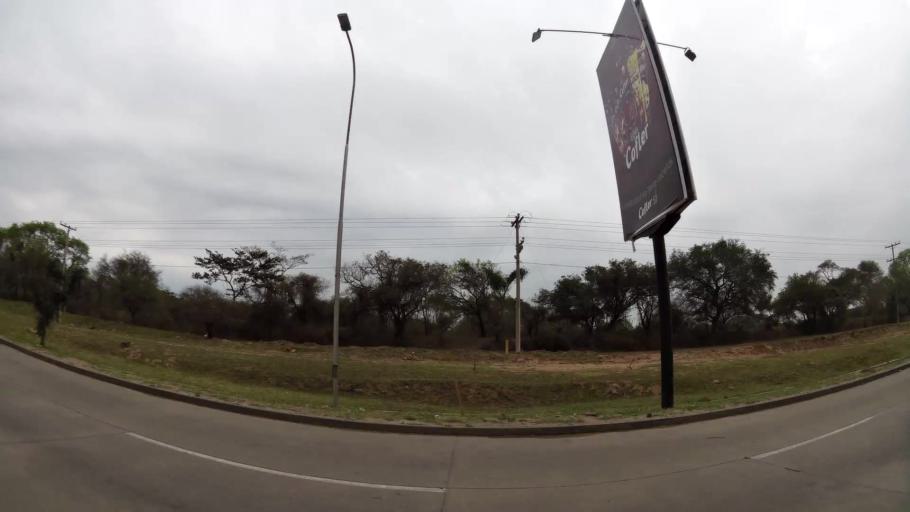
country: BO
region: Santa Cruz
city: Santa Cruz de la Sierra
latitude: -17.7605
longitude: -63.2025
